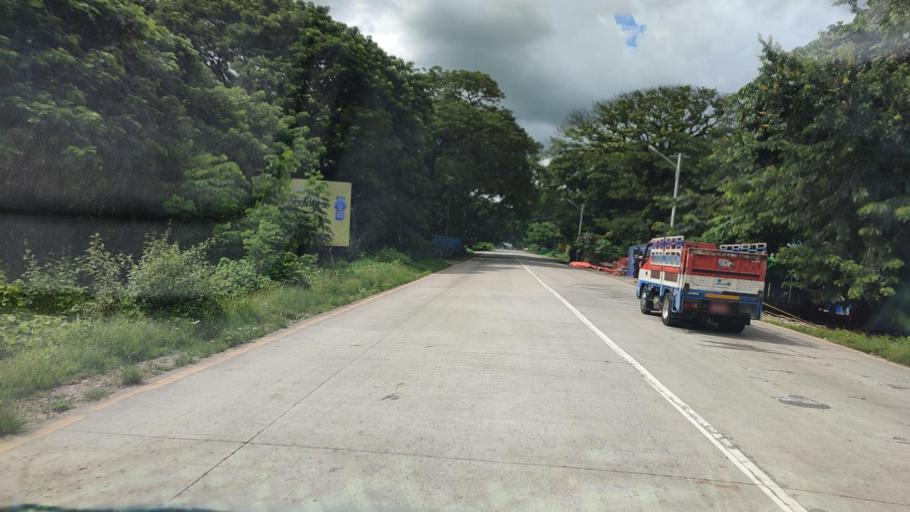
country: MM
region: Bago
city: Nyaunglebin
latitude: 17.9589
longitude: 96.7134
